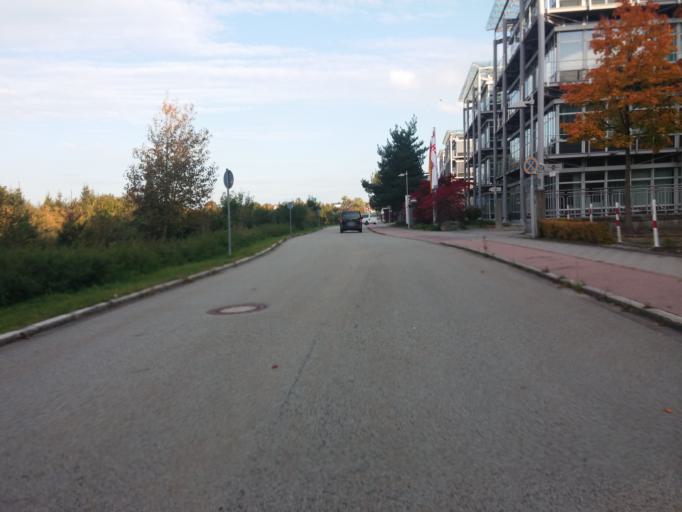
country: DE
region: Bavaria
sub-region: Upper Bavaria
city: Vaterstetten
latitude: 48.1025
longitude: 11.7571
